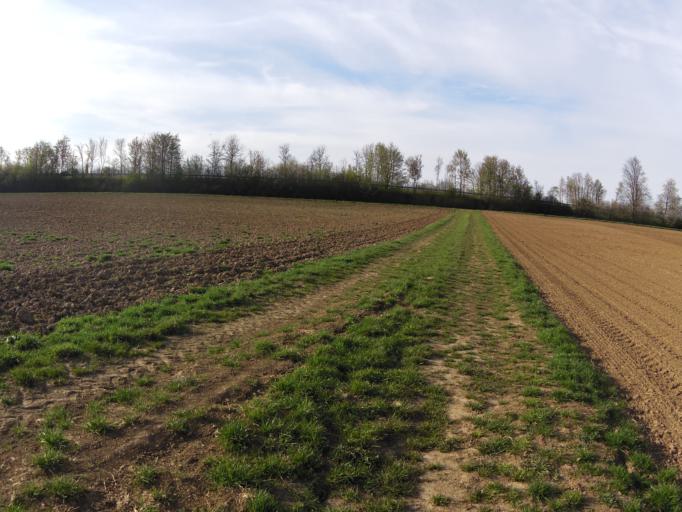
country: DE
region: Bavaria
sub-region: Regierungsbezirk Unterfranken
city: Biebelried
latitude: 49.7872
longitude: 10.0997
